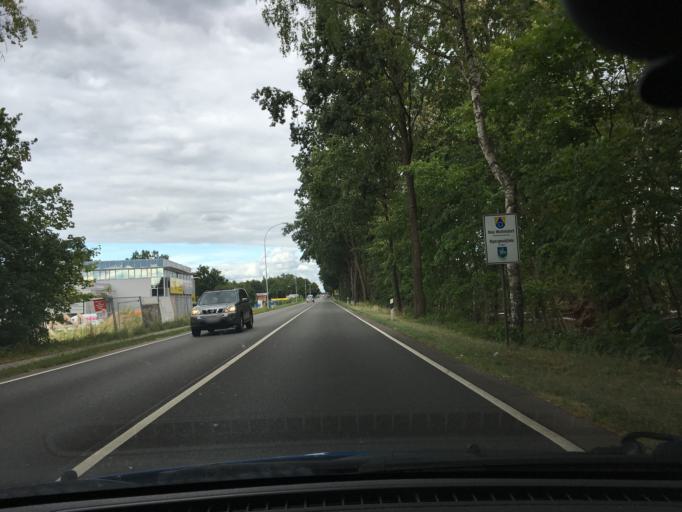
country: DE
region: Lower Saxony
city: Neu Wulmstorf
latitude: 53.4585
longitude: 9.7832
